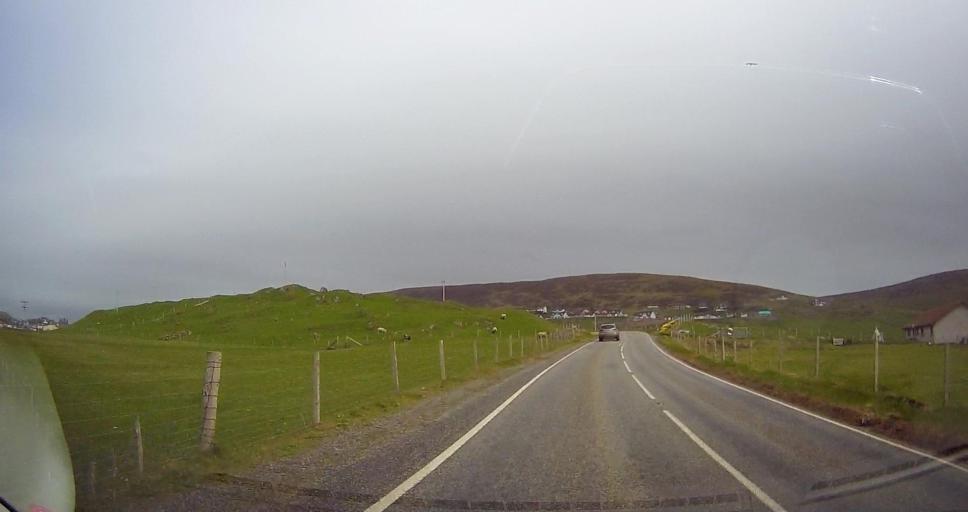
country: GB
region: Scotland
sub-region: Shetland Islands
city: Sandwick
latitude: 60.1264
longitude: -1.2815
